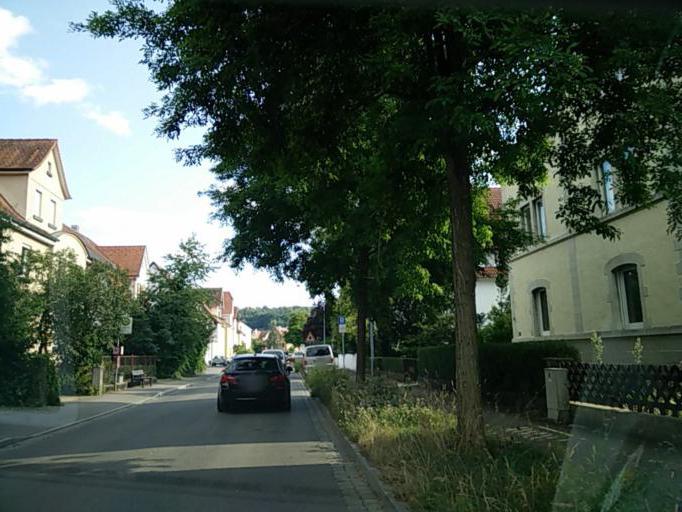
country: DE
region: Baden-Wuerttemberg
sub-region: Tuebingen Region
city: Tuebingen
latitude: 48.5072
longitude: 9.0512
